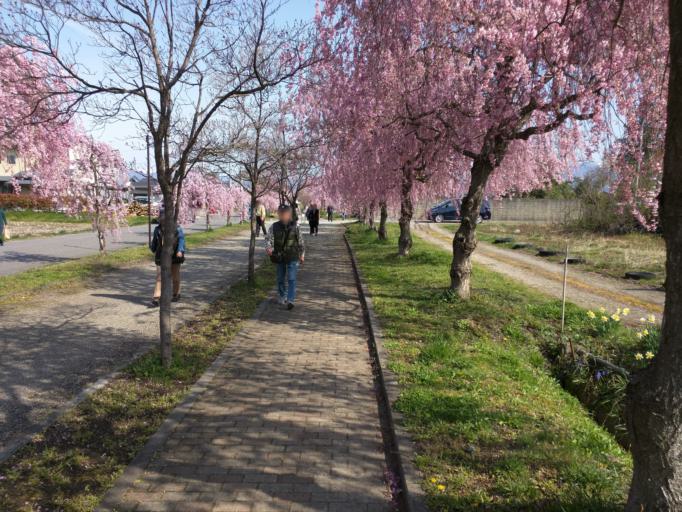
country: JP
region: Fukushima
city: Kitakata
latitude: 37.6666
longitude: 139.8709
